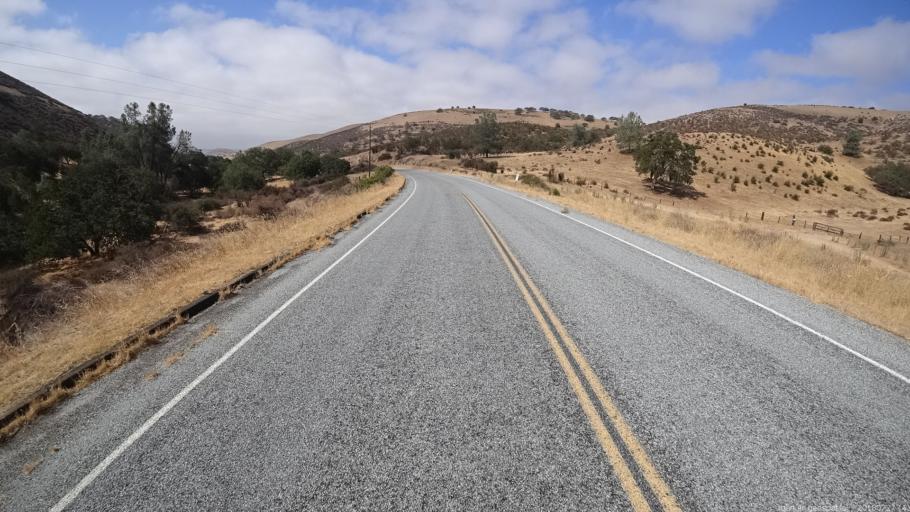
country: US
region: California
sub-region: Monterey County
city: King City
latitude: 36.2995
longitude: -121.0506
